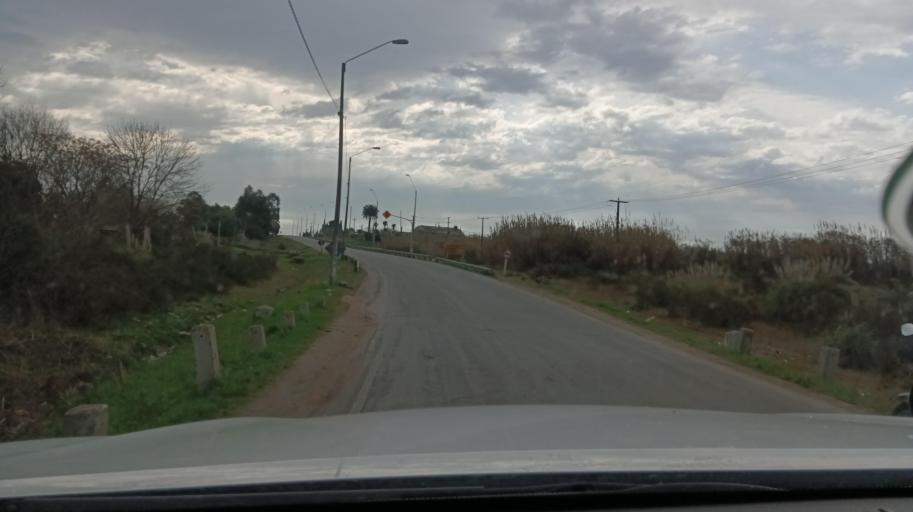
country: UY
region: Canelones
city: Toledo
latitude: -34.7511
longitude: -56.1088
